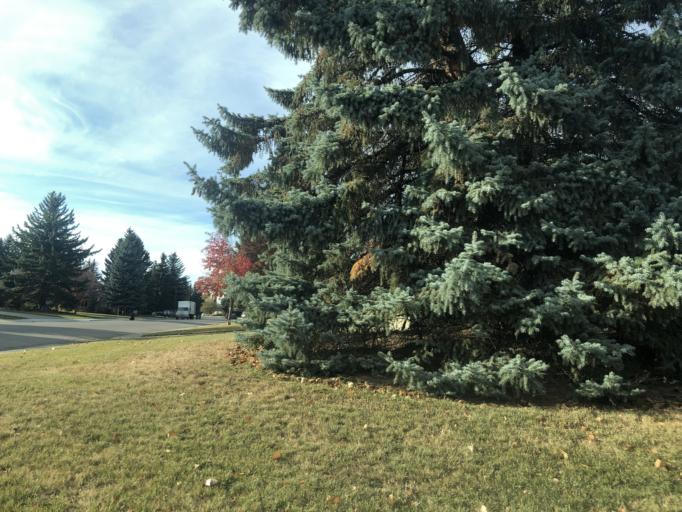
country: CA
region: Alberta
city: Calgary
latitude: 50.9363
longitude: -114.0551
